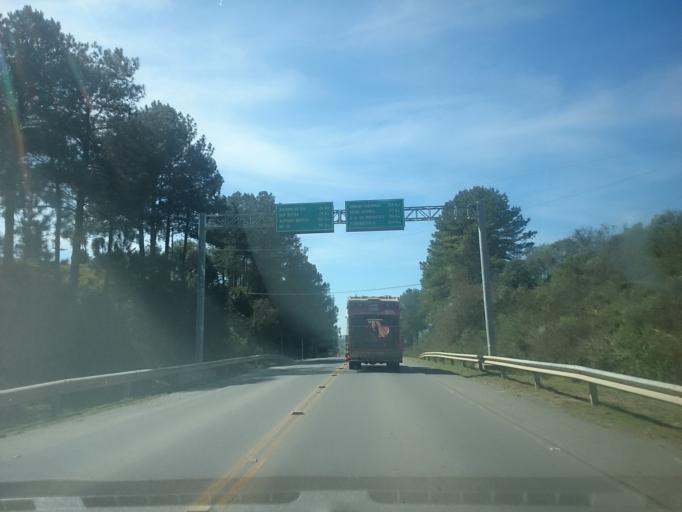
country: BR
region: Santa Catarina
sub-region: Lages
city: Lages
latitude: -27.7729
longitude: -50.1978
